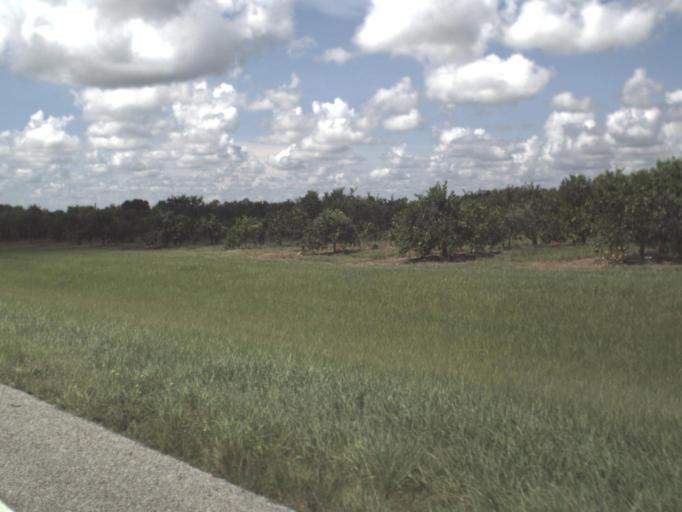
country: US
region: Florida
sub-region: DeSoto County
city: Arcadia
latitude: 27.2925
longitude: -81.8265
